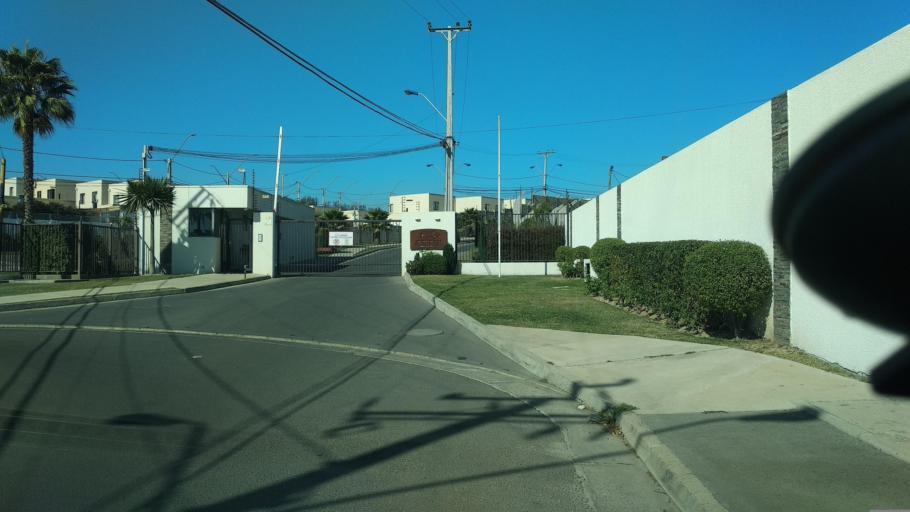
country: CL
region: Valparaiso
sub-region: Provincia de Marga Marga
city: Villa Alemana
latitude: -33.0349
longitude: -71.3871
